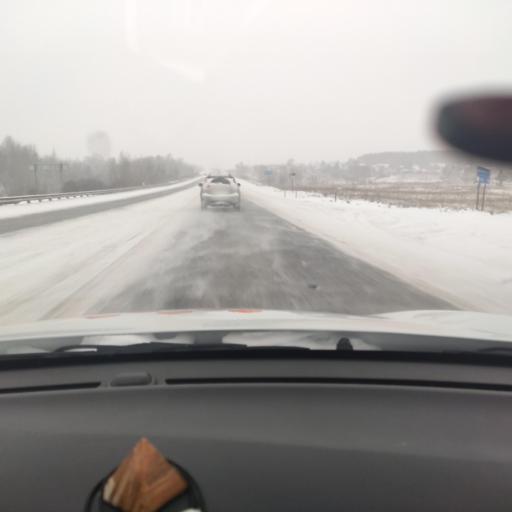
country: RU
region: Tatarstan
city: Verkhniy Uslon
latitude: 55.7195
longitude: 48.8394
